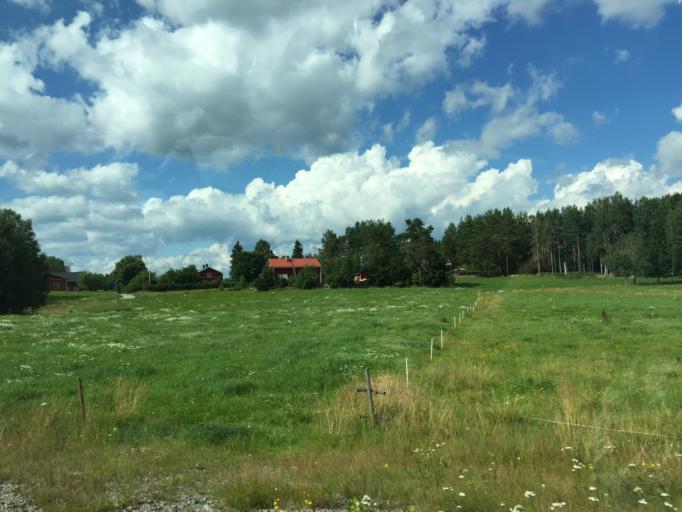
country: SE
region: Gaevleborg
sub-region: Bollnas Kommun
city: Kilafors
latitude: 61.2144
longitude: 16.6487
